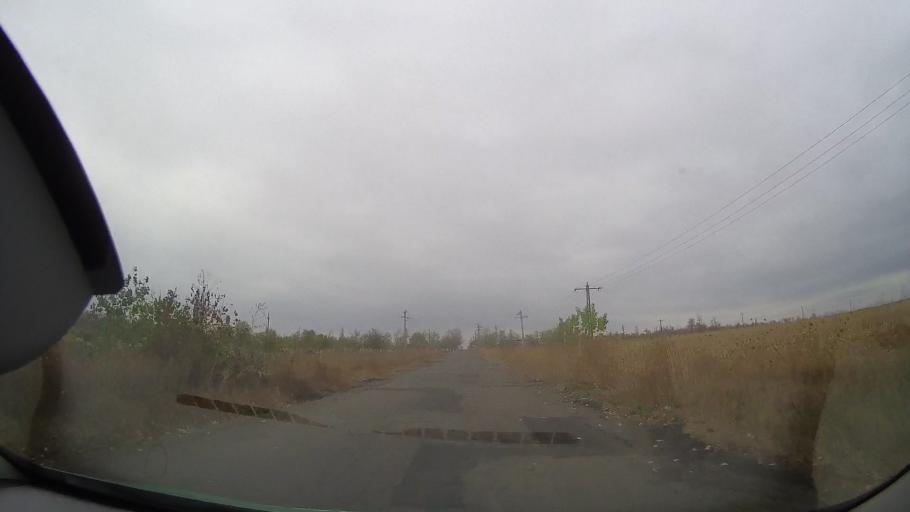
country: RO
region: Braila
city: Dudesti
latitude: 44.9392
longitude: 27.4251
